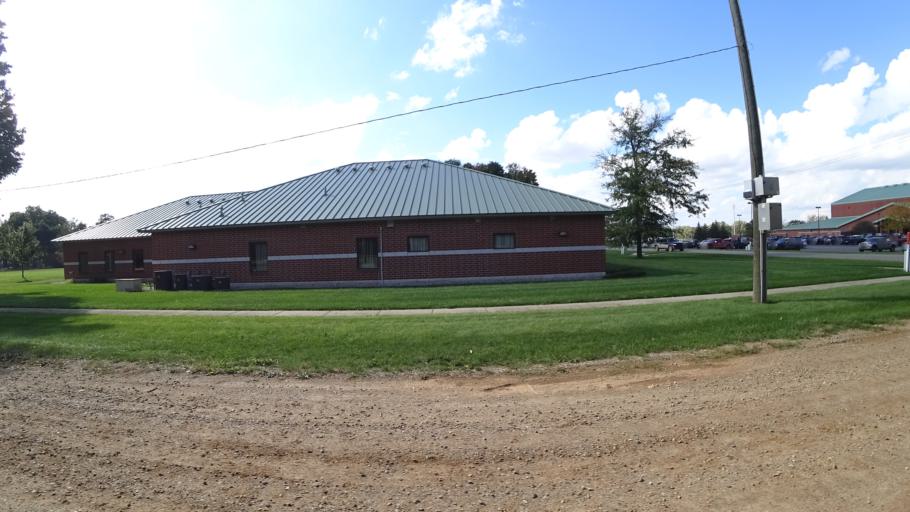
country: US
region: Michigan
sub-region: Saint Joseph County
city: Three Rivers
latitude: 41.9472
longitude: -85.6152
